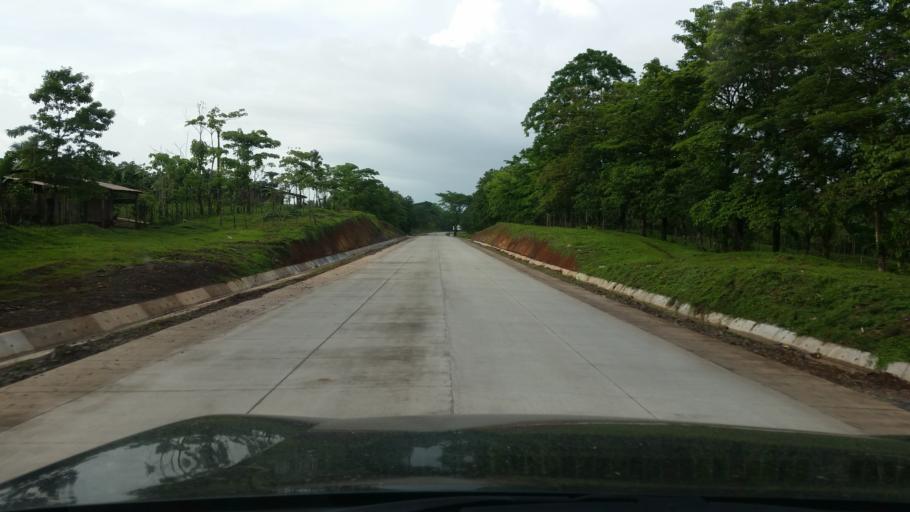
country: NI
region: Matagalpa
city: Rio Blanco
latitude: 13.1067
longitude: -85.0658
